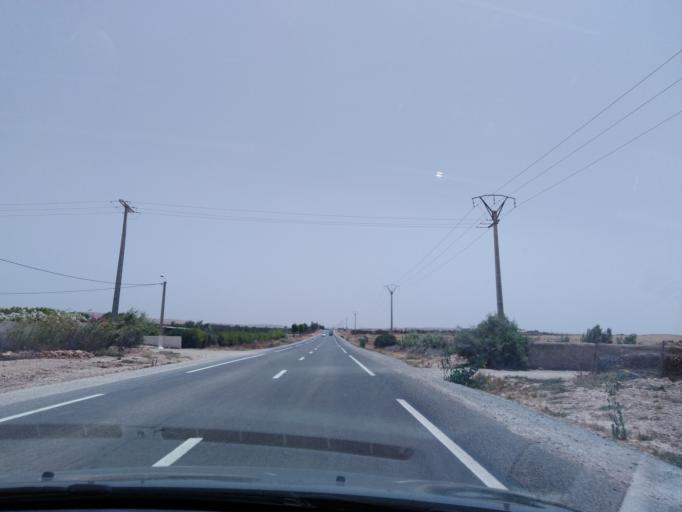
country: MA
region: Doukkala-Abda
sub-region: Safi
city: Youssoufia
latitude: 32.0564
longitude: -8.5634
